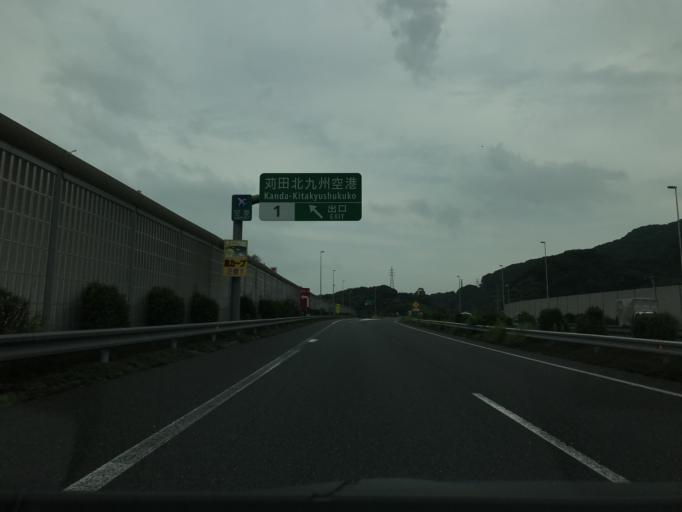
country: JP
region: Fukuoka
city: Kanda
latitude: 33.7970
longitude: 130.9636
